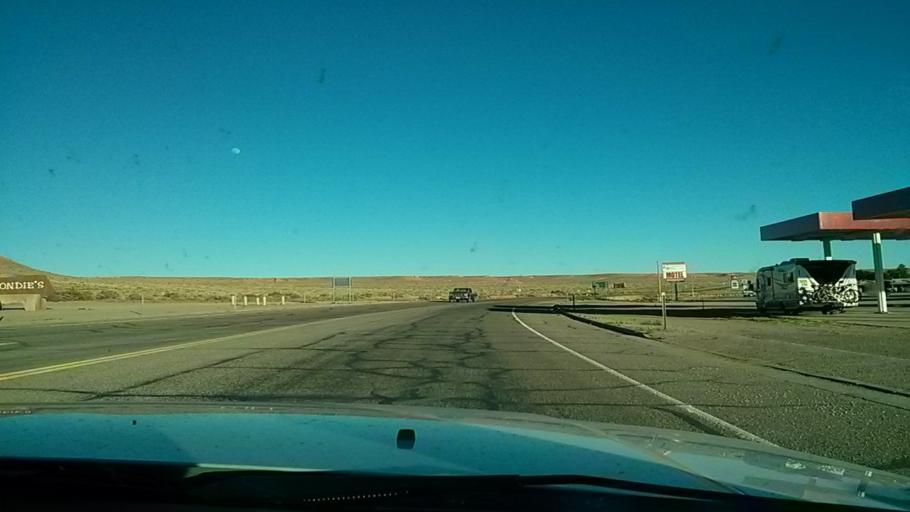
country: US
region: Utah
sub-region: Emery County
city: Ferron
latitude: 38.3734
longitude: -110.7050
